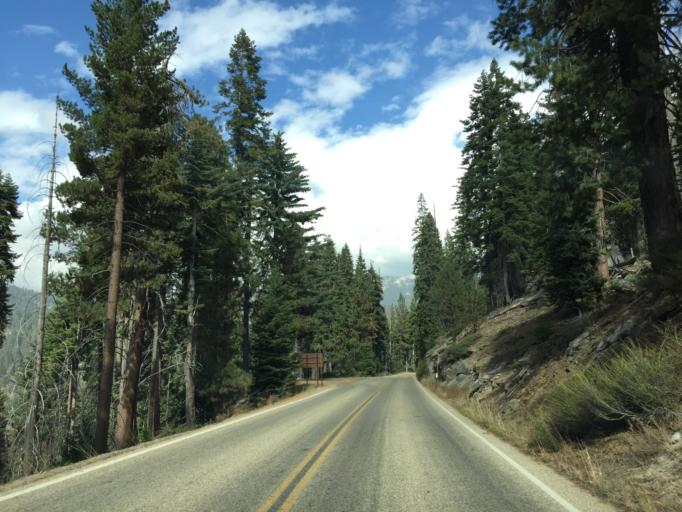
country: US
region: California
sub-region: Tulare County
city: Three Rivers
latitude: 36.5912
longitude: -118.7520
